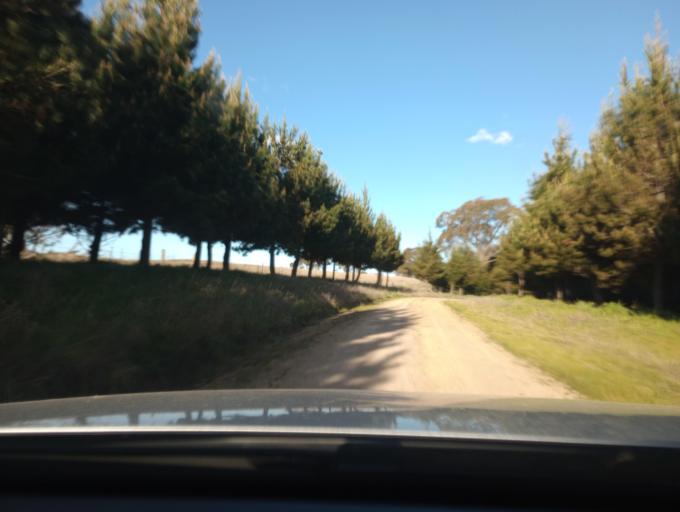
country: AU
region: New South Wales
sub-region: Blayney
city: Millthorpe
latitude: -33.3969
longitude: 149.3101
